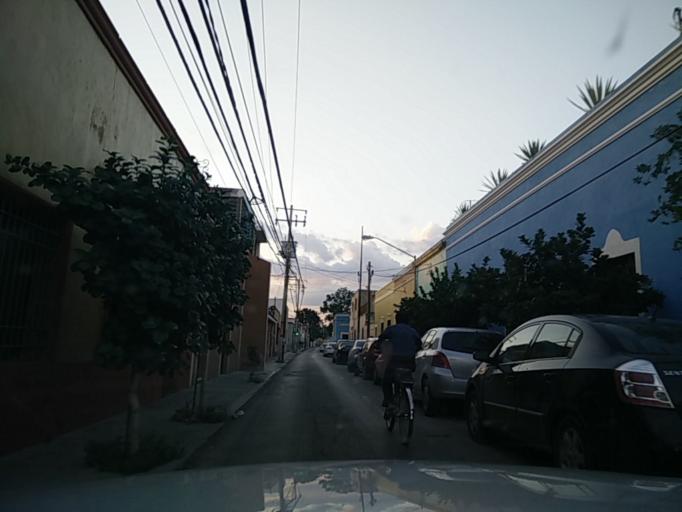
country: MX
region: Yucatan
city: Merida
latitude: 20.9724
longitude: -89.6241
